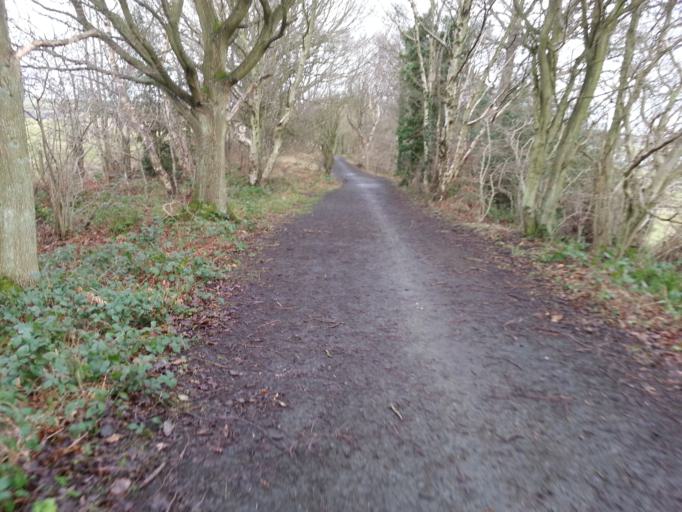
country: GB
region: England
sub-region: County Durham
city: Crook
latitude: 54.7549
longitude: -1.7315
